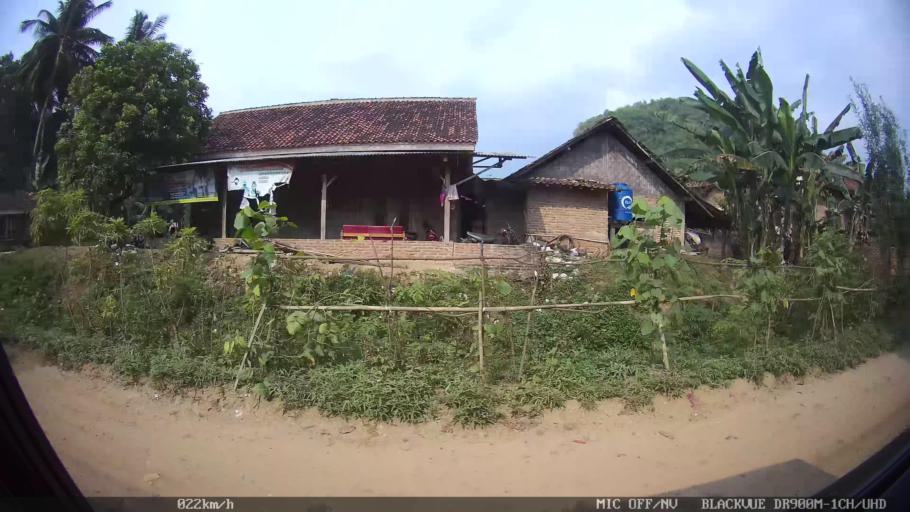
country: ID
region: Lampung
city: Gadingrejo
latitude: -5.3865
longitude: 105.0186
